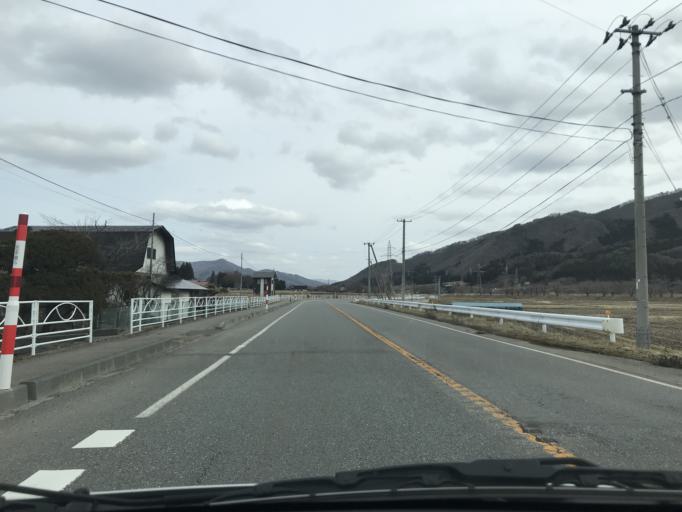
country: JP
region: Iwate
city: Tono
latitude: 39.3092
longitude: 141.4294
